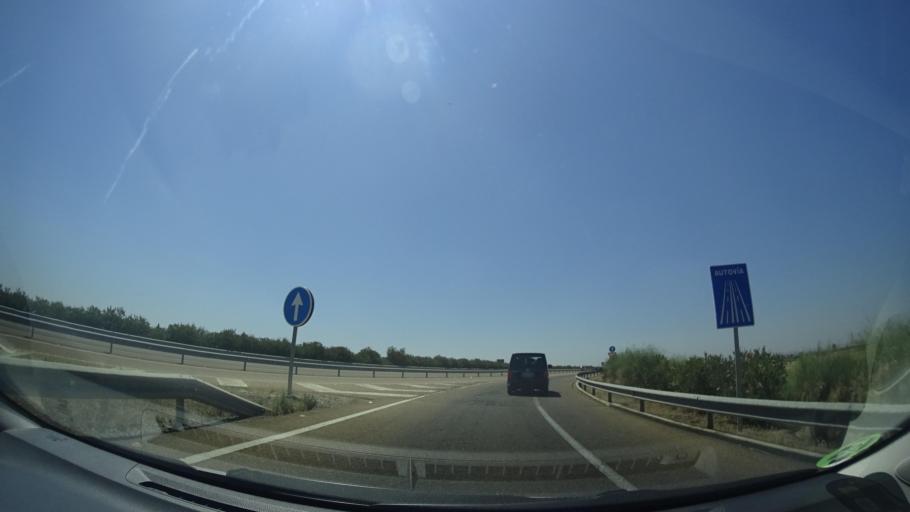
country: ES
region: Extremadura
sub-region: Provincia de Badajoz
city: Puebla de Sancho Perez
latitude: 38.3949
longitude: -6.3410
